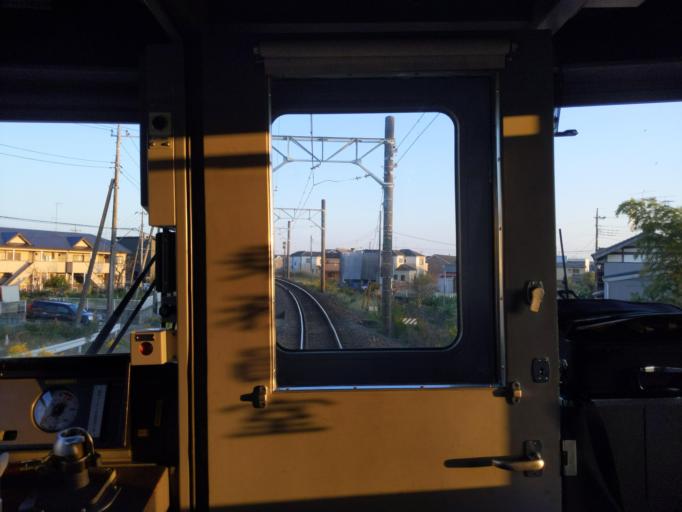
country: JP
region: Saitama
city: Kasukabe
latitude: 35.9759
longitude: 139.7597
